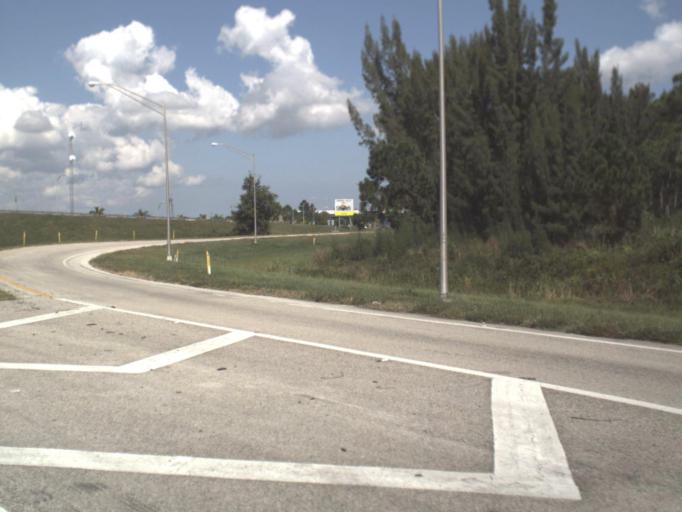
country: US
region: Florida
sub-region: Martin County
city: Palm City
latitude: 27.1564
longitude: -80.3011
